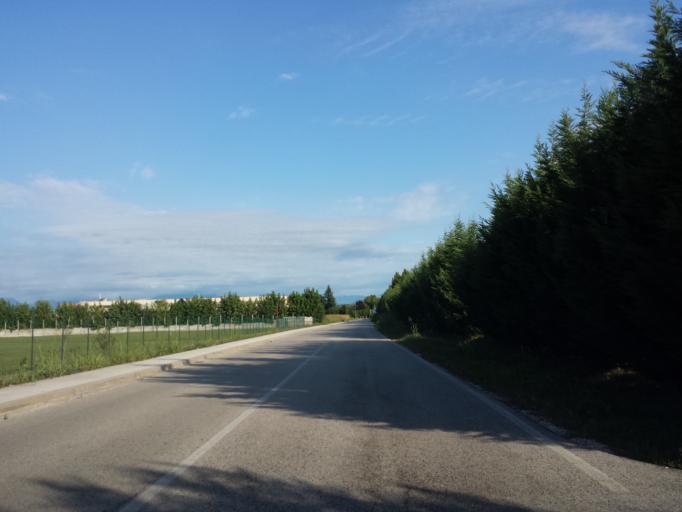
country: IT
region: Veneto
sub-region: Provincia di Vicenza
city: Torri di Quartesolo
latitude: 45.5214
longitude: 11.5970
